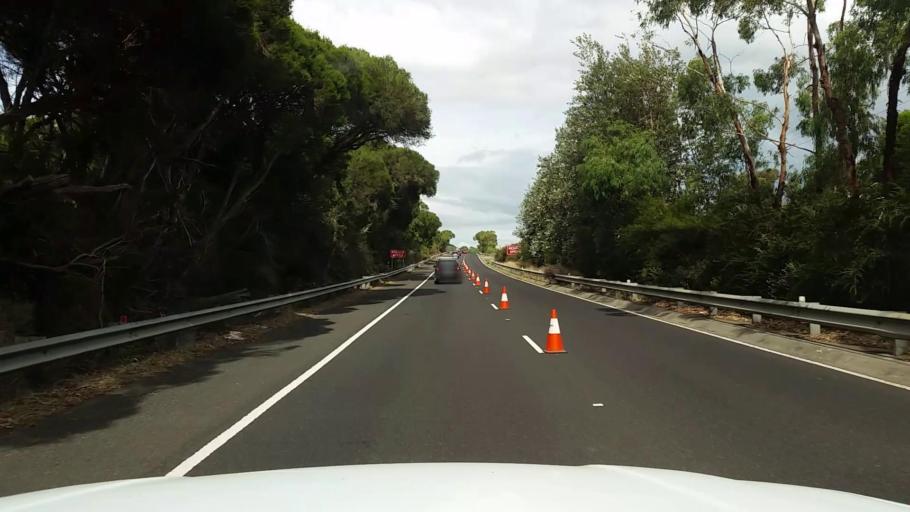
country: AU
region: Victoria
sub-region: Frankston
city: Frankston East
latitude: -38.1402
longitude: 145.1368
